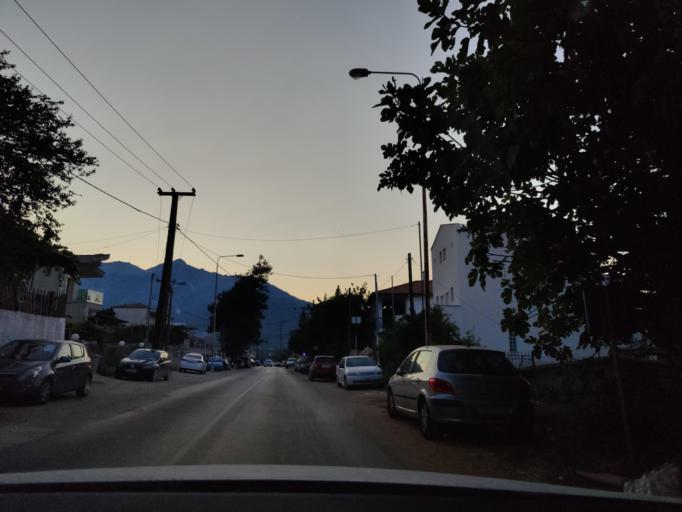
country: GR
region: East Macedonia and Thrace
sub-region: Nomos Kavalas
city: Potamia
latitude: 40.7076
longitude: 24.7583
